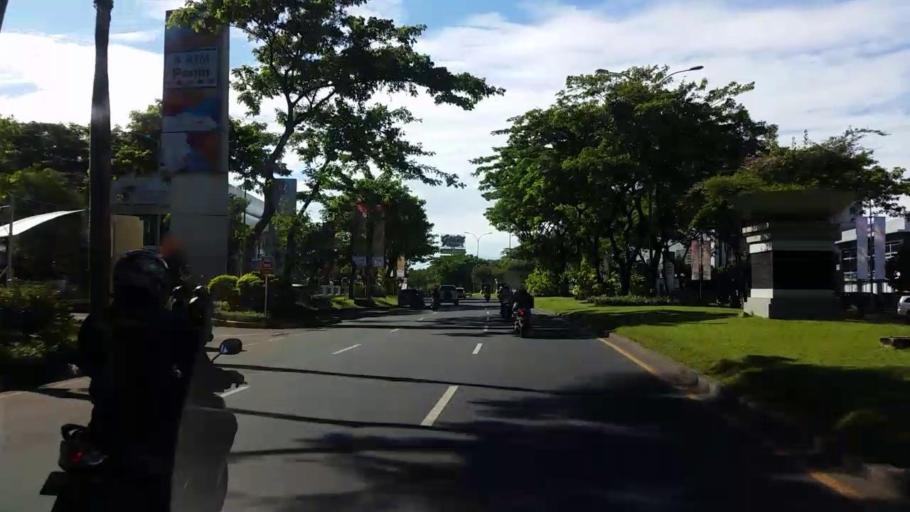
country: ID
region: West Java
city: Serpong
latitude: -6.2956
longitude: 106.6665
